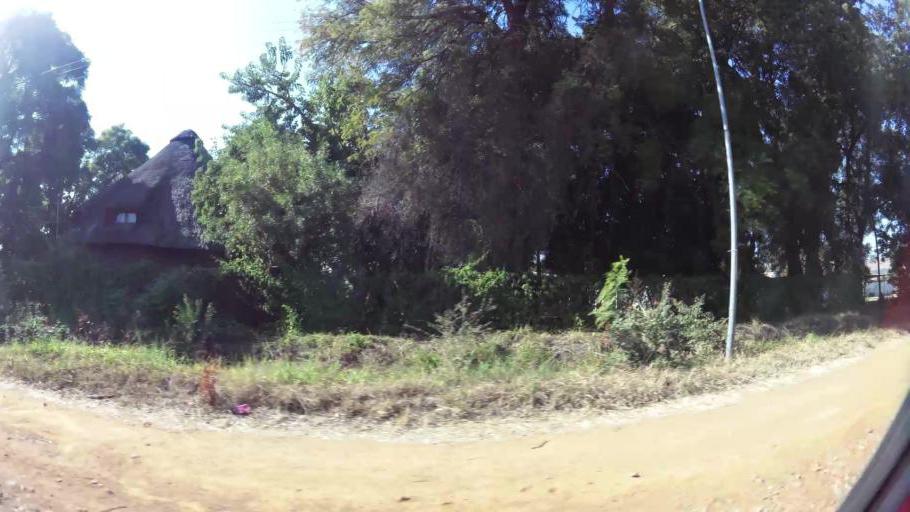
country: ZA
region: North-West
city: Ga-Rankuwa
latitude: -25.6643
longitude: 28.1014
